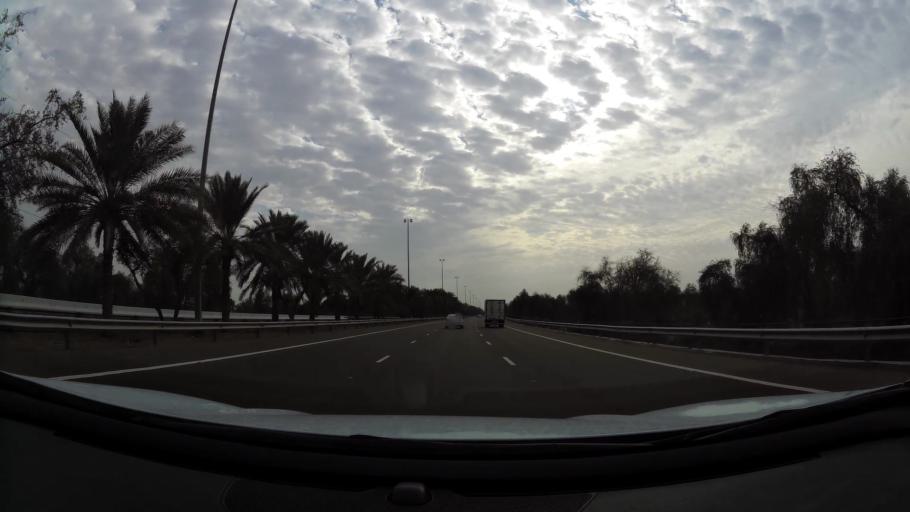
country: AE
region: Abu Dhabi
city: Al Ain
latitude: 24.1718
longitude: 55.2356
